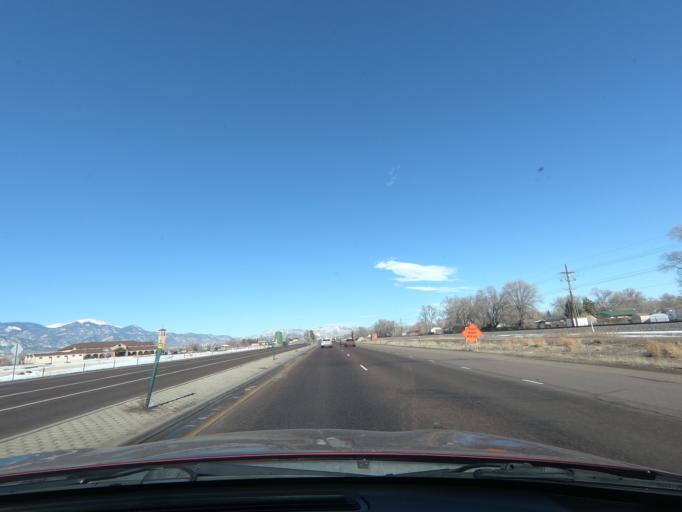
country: US
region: Colorado
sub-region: El Paso County
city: Security-Widefield
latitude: 38.7524
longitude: -104.7451
